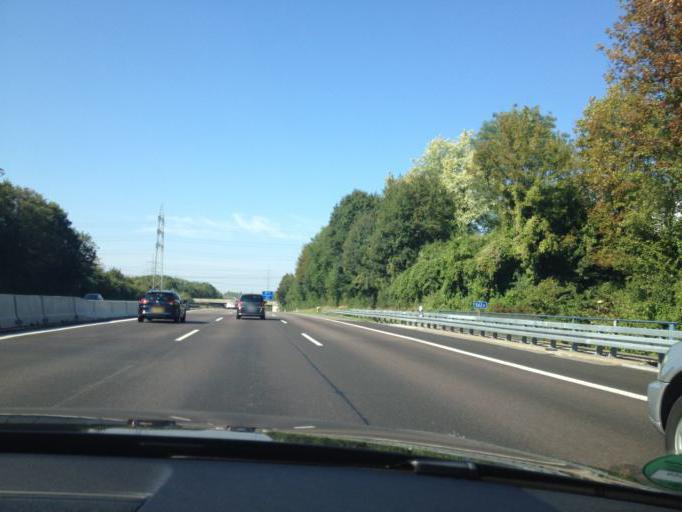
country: DE
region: Baden-Wuerttemberg
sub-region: Regierungsbezirk Stuttgart
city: Freiberg am Neckar
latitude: 48.9311
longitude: 9.1800
